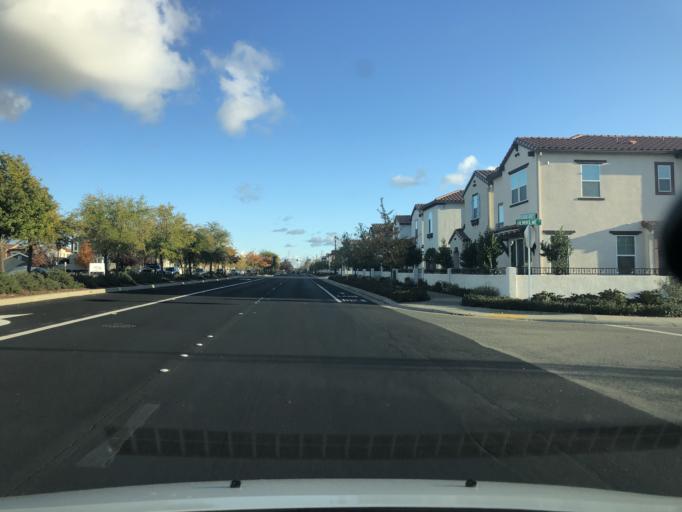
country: US
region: California
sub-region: Sacramento County
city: Antelope
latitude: 38.7715
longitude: -121.3694
